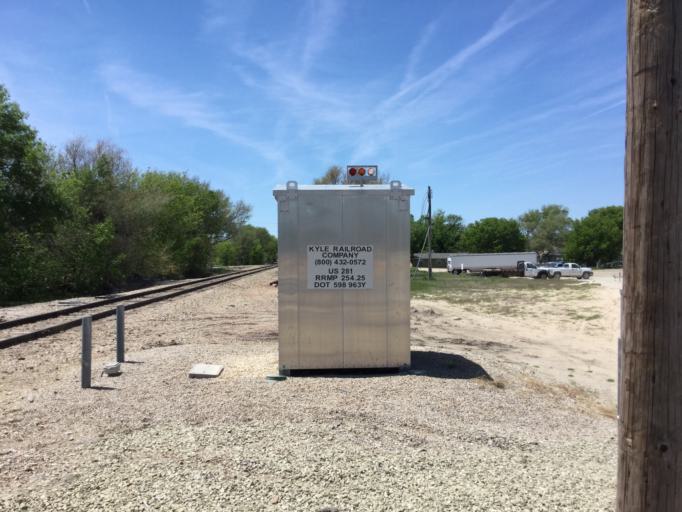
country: US
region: Kansas
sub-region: Smith County
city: Smith Center
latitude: 39.7745
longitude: -98.7859
